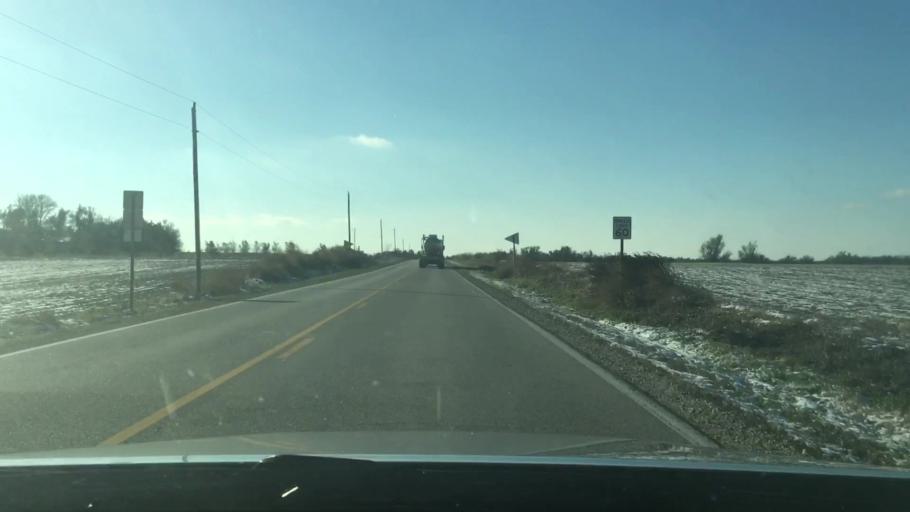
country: US
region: Kansas
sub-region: Rice County
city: Sterling
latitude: 38.1445
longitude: -98.1823
